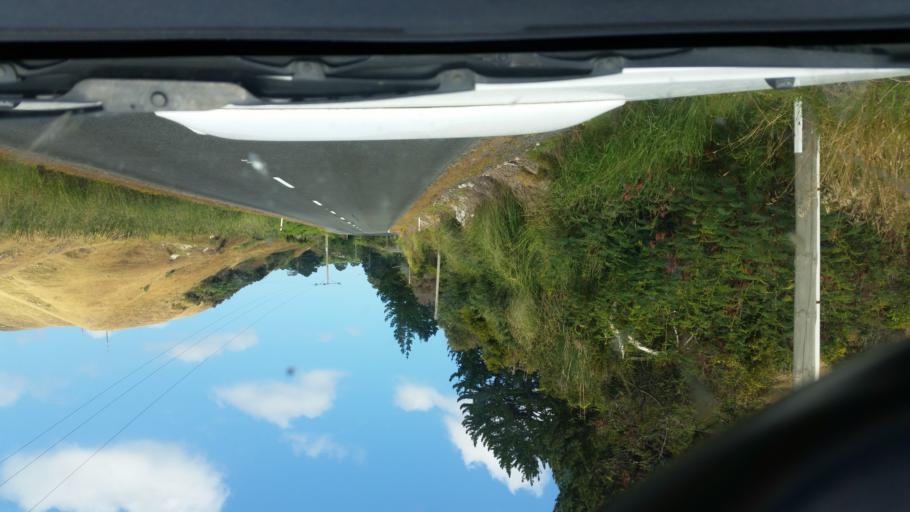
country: NZ
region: Northland
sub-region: Kaipara District
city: Dargaville
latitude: -35.8225
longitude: 173.6992
